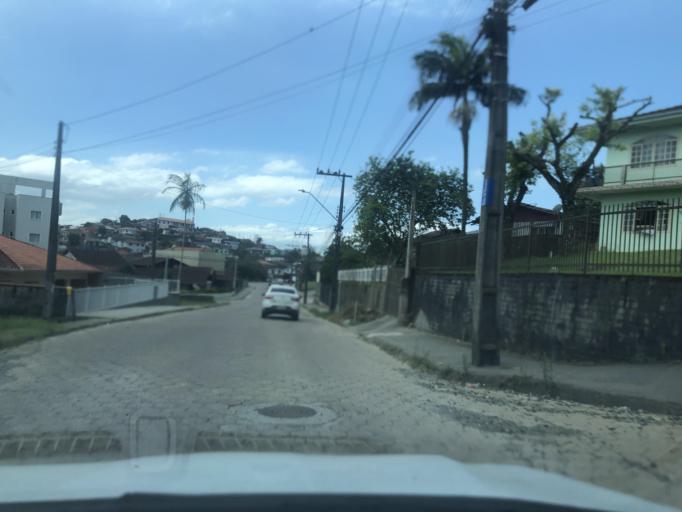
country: BR
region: Santa Catarina
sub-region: Joinville
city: Joinville
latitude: -26.3384
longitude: -48.8090
